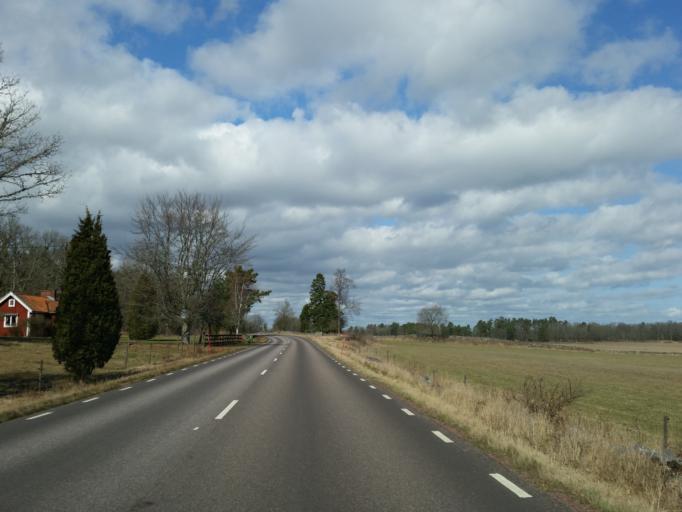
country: SE
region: Kalmar
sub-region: Monsteras Kommun
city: Timmernabben
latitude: 56.9219
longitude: 16.4215
